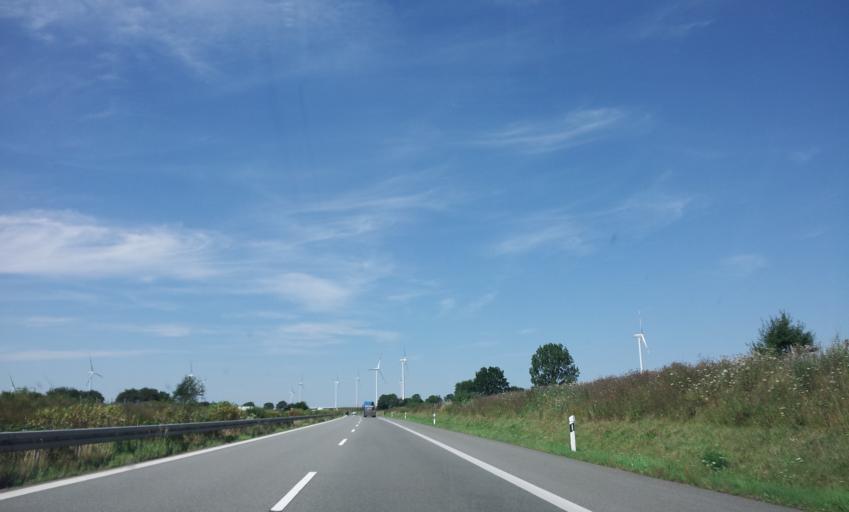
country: DE
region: Mecklenburg-Vorpommern
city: Dersekow
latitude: 54.0404
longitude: 13.2670
